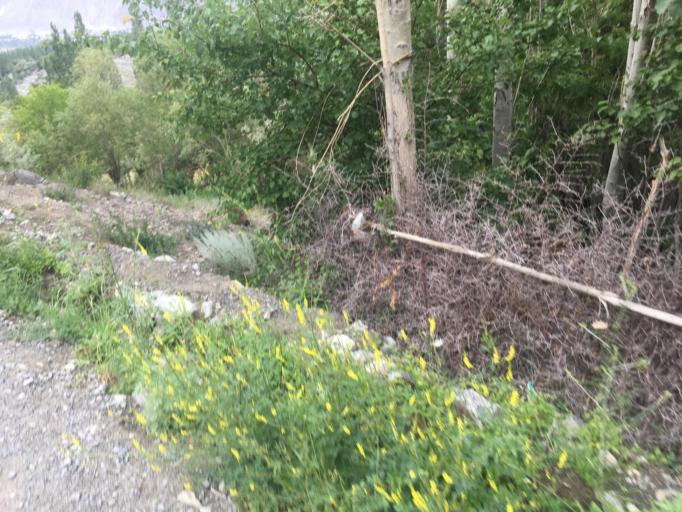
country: PK
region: Gilgit-Baltistan
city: Skardu
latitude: 35.2665
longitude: 75.6344
